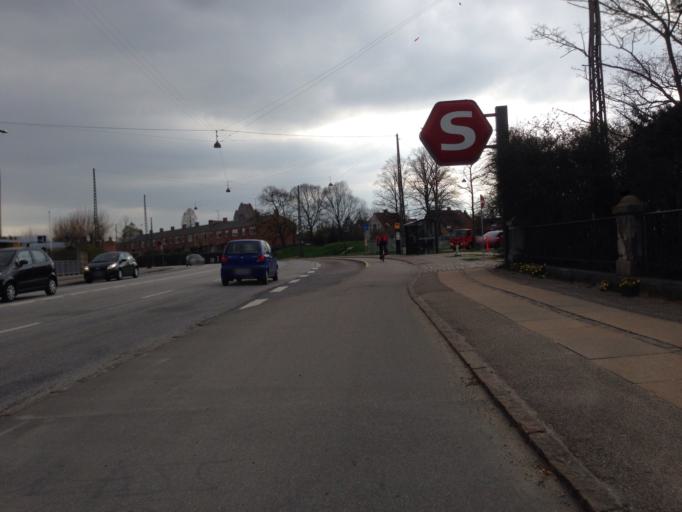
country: DK
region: Capital Region
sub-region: Frederiksberg Kommune
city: Frederiksberg
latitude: 55.7197
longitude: 12.5419
